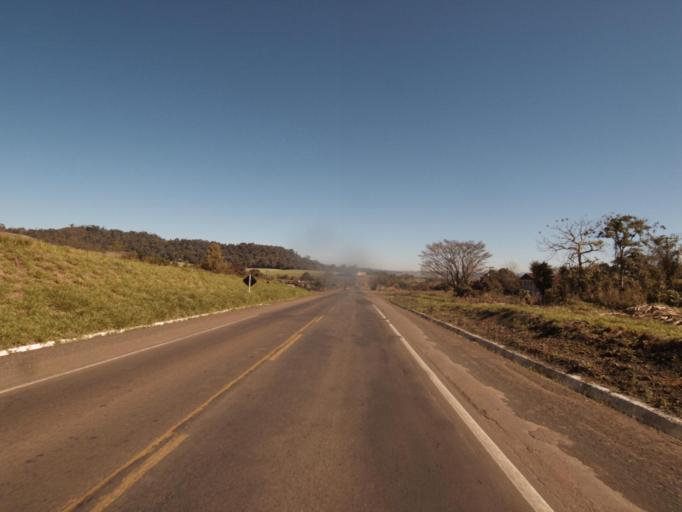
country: BR
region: Rio Grande do Sul
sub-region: Frederico Westphalen
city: Frederico Westphalen
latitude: -26.7996
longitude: -53.3501
